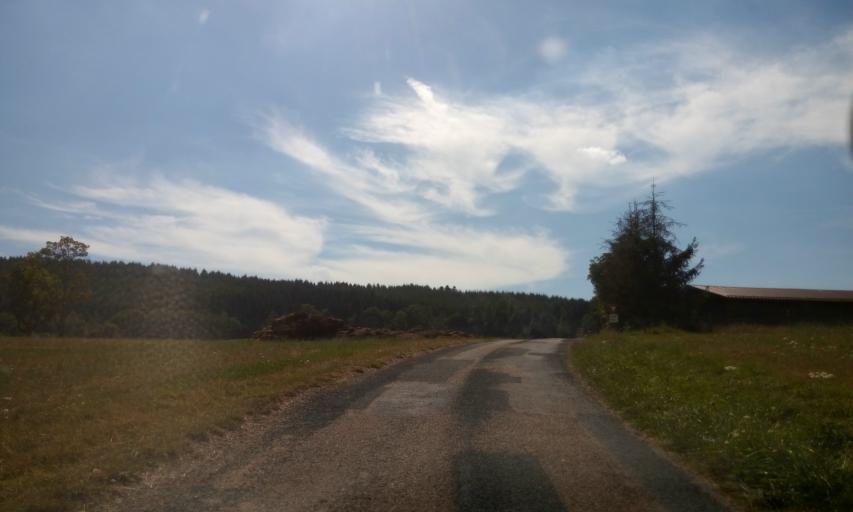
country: FR
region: Rhone-Alpes
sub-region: Departement du Rhone
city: Cublize
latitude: 45.9810
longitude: 4.3893
